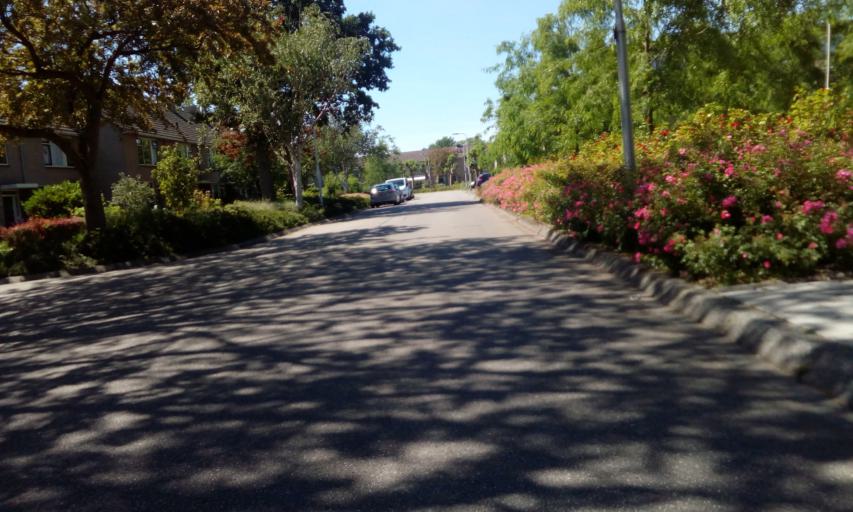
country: NL
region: South Holland
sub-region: Gemeente Lansingerland
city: Bleiswijk
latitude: 52.0076
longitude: 4.5394
